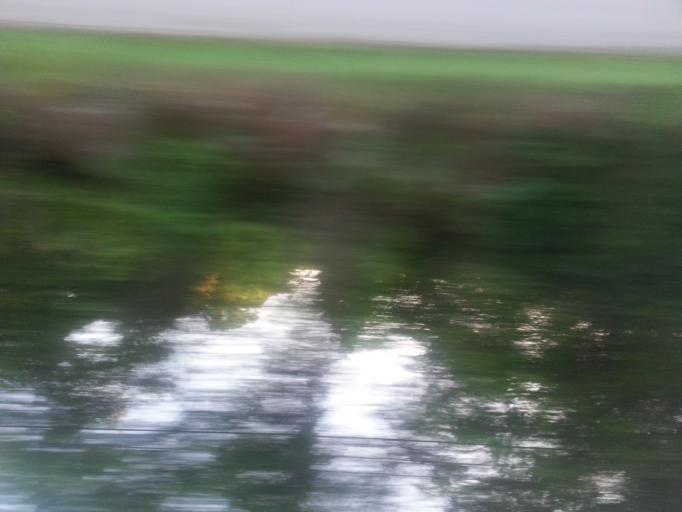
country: US
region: Tennessee
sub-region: Knox County
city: Mascot
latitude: 36.0239
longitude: -83.7528
